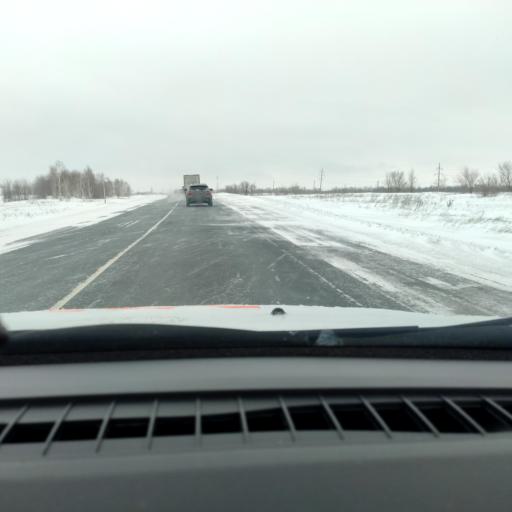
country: RU
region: Samara
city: Chapayevsk
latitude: 53.0245
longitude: 49.7762
